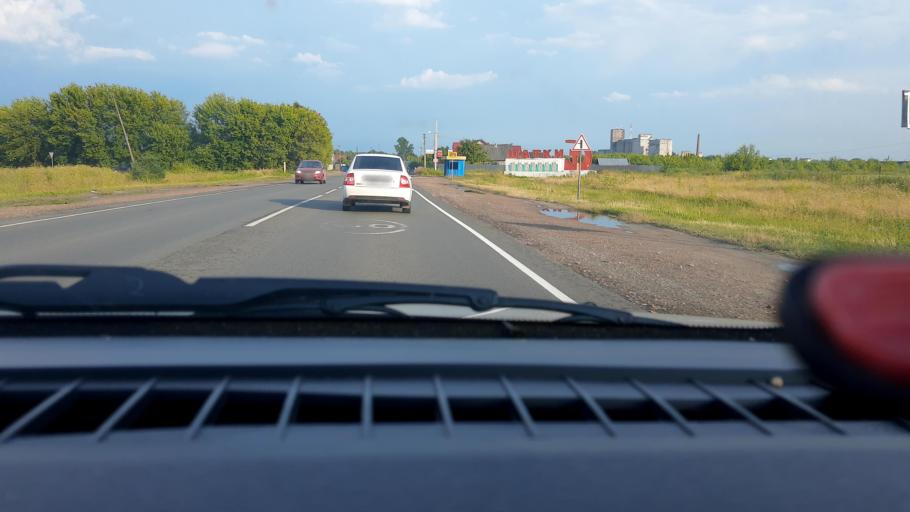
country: RU
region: Nizjnij Novgorod
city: Shatki
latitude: 55.2053
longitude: 44.0955
